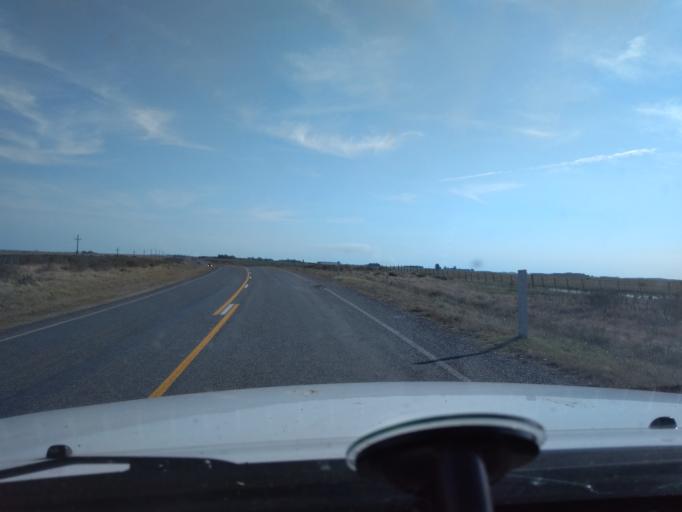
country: UY
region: Florida
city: Casupa
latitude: -34.0007
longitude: -55.7882
